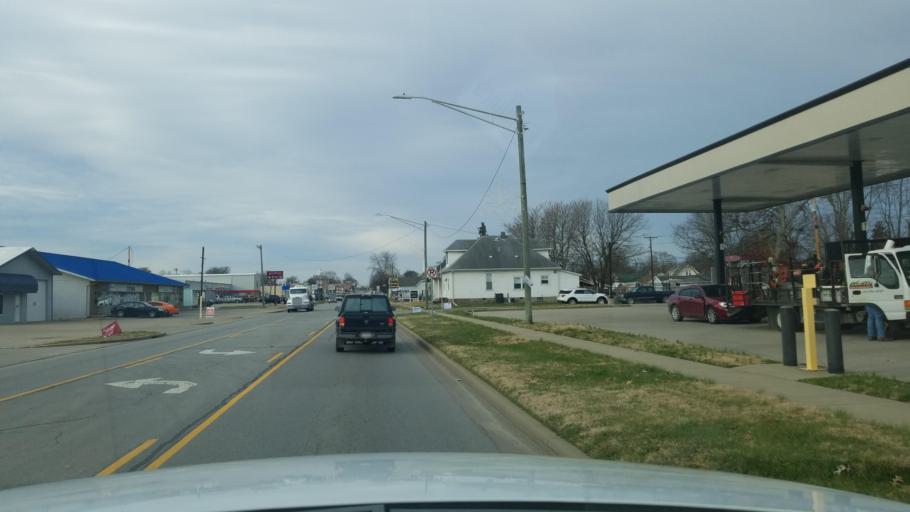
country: US
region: Indiana
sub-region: Posey County
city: Mount Vernon
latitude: 37.9351
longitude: -87.8845
